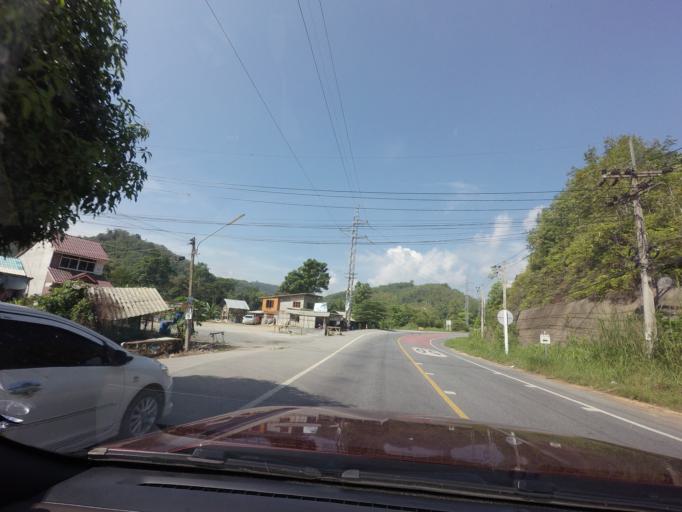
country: TH
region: Yala
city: Than To
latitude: 5.9600
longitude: 101.1942
